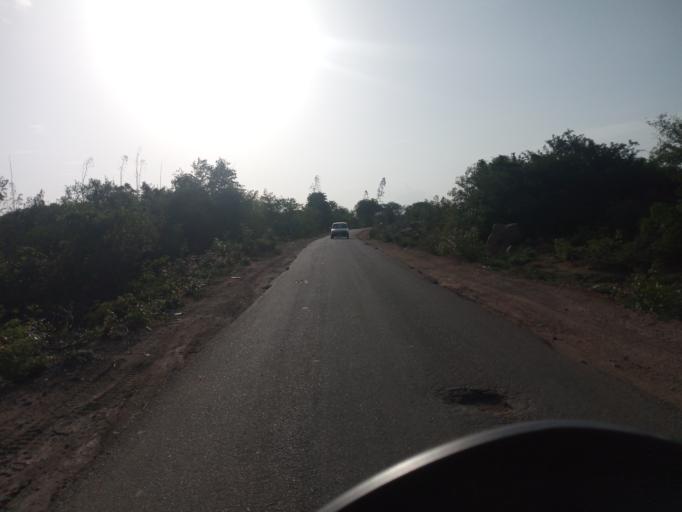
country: IN
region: Telangana
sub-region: Rangareddi
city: Quthbullapur
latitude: 17.5554
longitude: 78.4136
